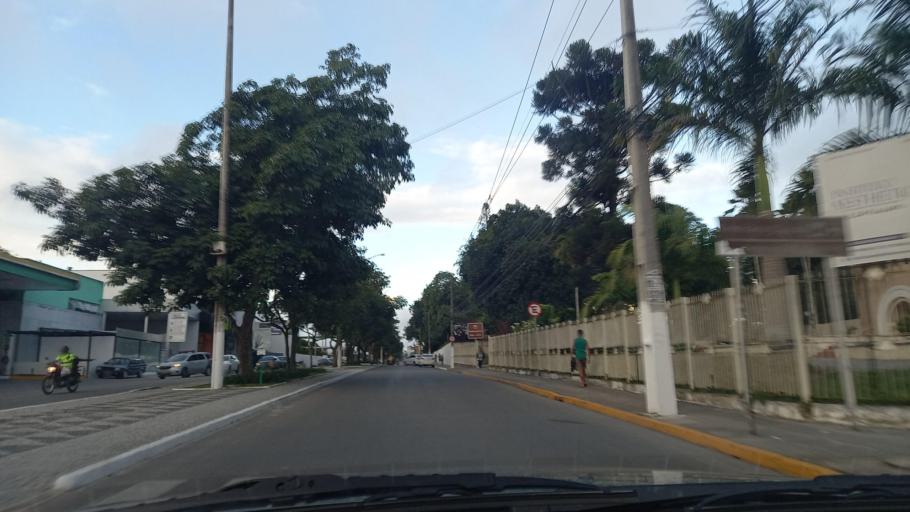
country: BR
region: Pernambuco
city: Garanhuns
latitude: -8.8865
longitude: -36.4861
